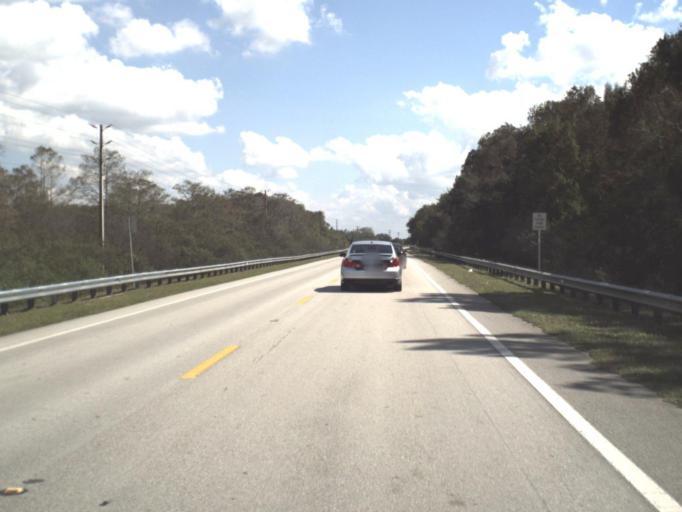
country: US
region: Florida
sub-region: Okeechobee County
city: Okeechobee
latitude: 27.3798
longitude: -80.9893
